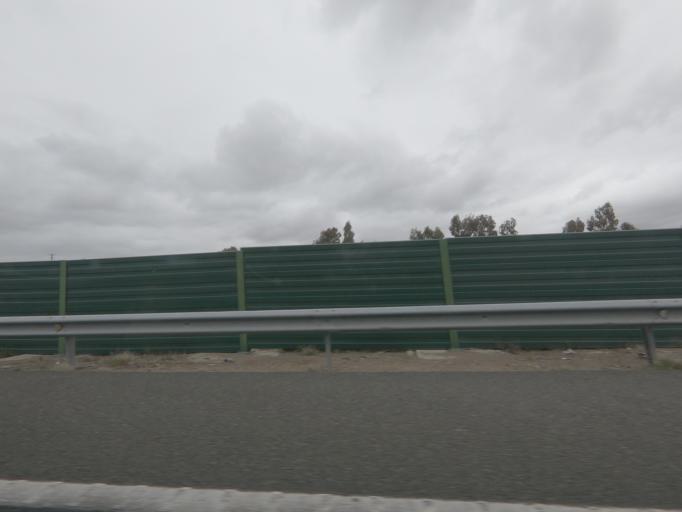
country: ES
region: Extremadura
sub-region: Provincia de Caceres
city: Mirabel
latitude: 39.9148
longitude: -6.2460
